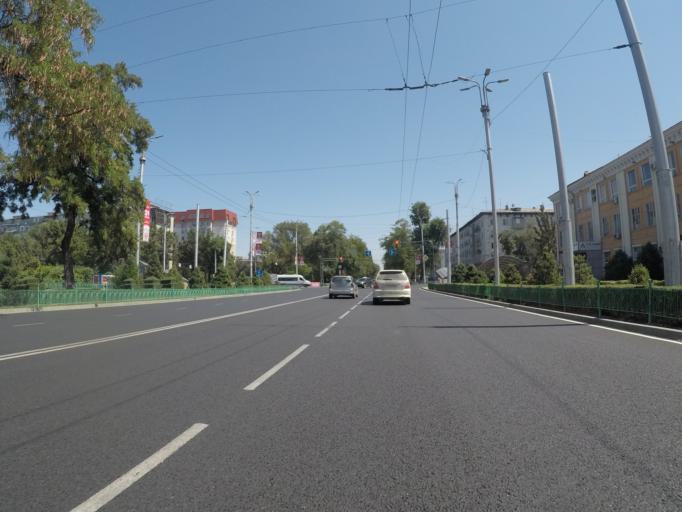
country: KG
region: Chuy
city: Bishkek
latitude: 42.8766
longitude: 74.5873
